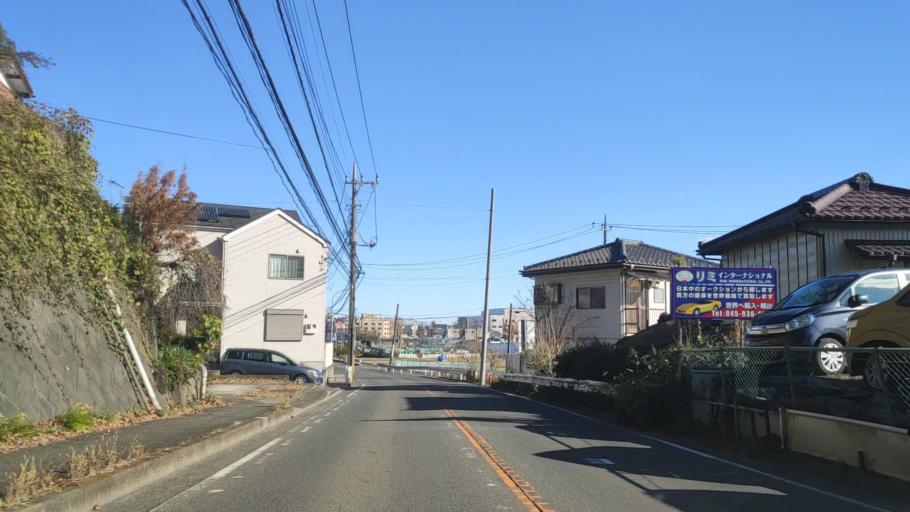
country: JP
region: Tokyo
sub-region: Machida-shi
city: Machida
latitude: 35.5189
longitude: 139.5392
